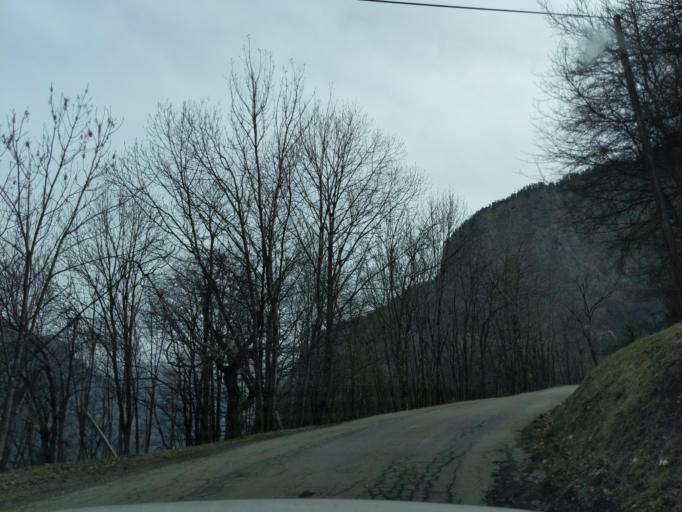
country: FR
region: Rhone-Alpes
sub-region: Departement de la Savoie
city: Villargondran
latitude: 45.2558
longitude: 6.3663
